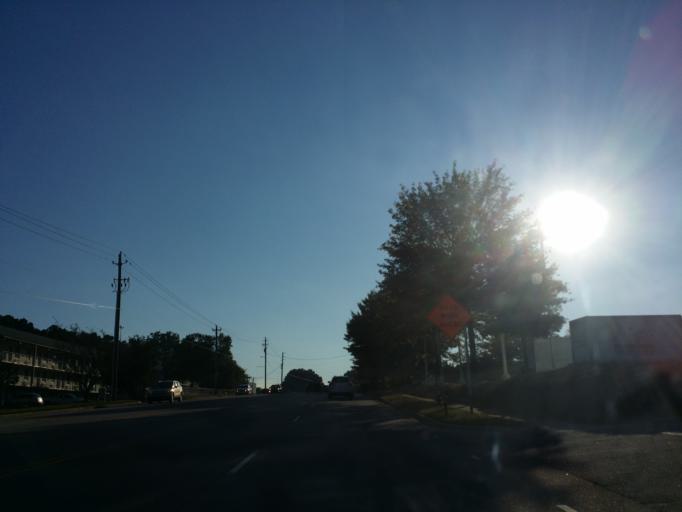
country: US
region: North Carolina
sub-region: Wake County
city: Cary
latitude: 35.7652
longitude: -78.7430
